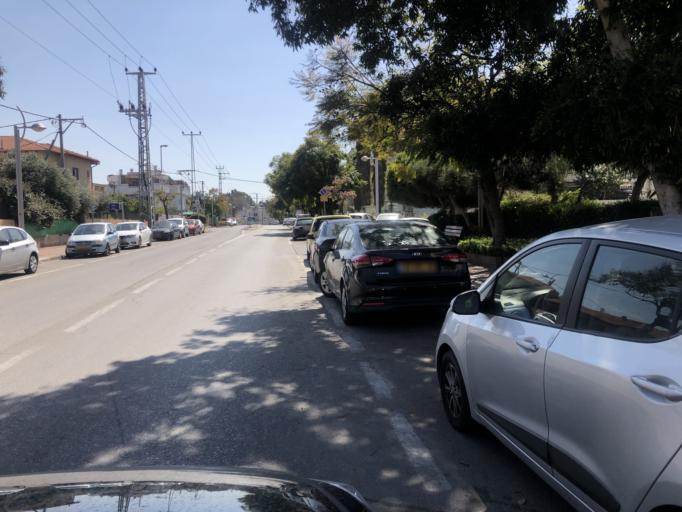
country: IL
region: Tel Aviv
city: Holon
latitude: 32.0086
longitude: 34.7647
